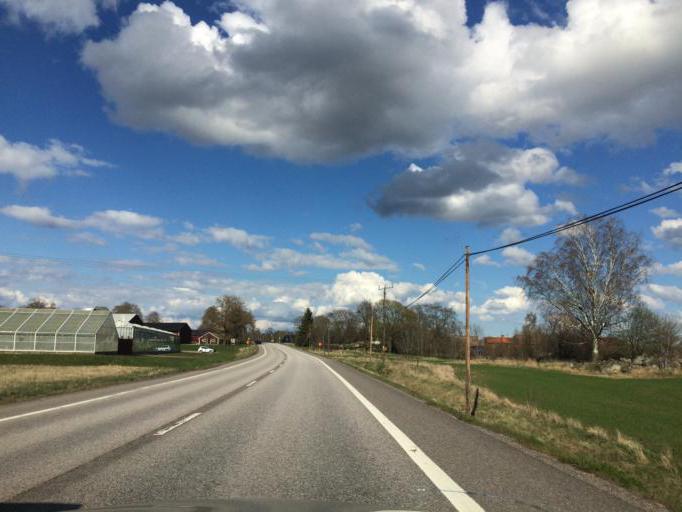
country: SE
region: Soedermanland
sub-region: Eskilstuna Kommun
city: Eskilstuna
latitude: 59.4233
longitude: 16.6039
